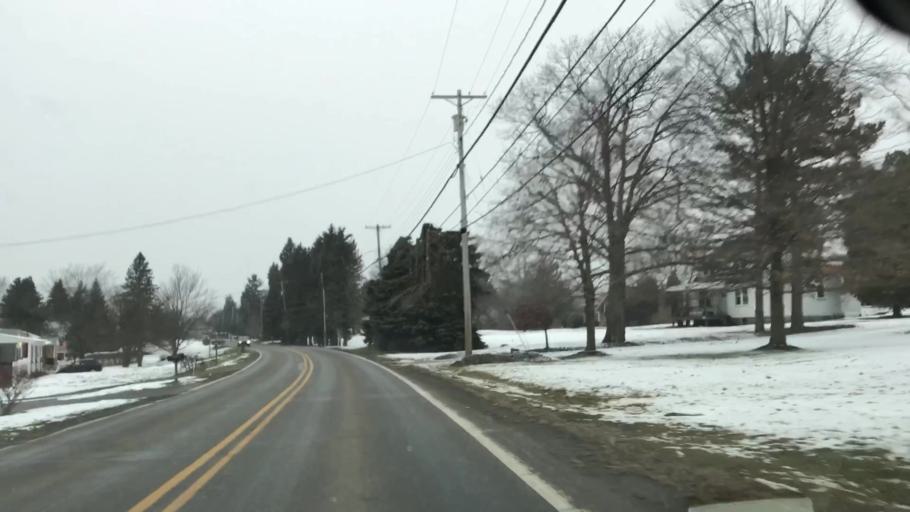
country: US
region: Pennsylvania
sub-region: Beaver County
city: Industry
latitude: 40.7008
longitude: -80.3952
